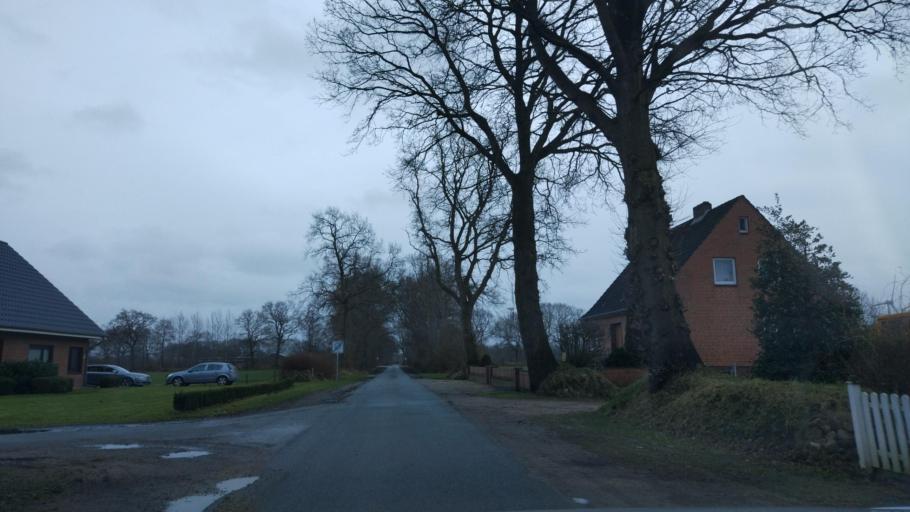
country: DE
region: Schleswig-Holstein
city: Klein Bennebek
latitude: 54.4011
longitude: 9.4572
